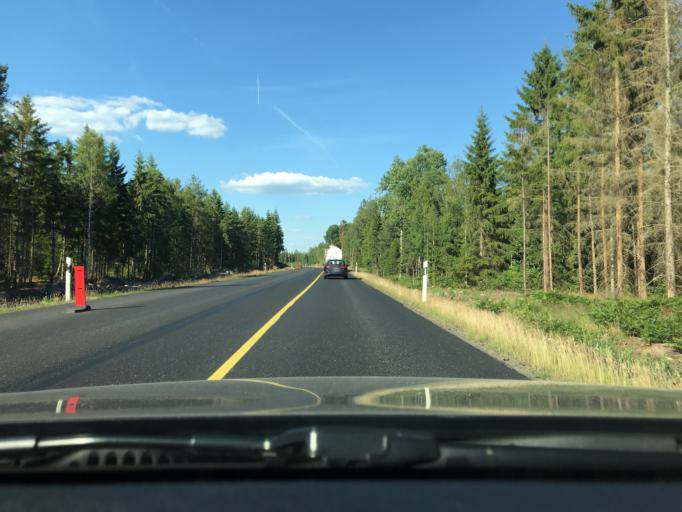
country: SE
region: Kronoberg
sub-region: Almhults Kommun
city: AElmhult
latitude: 56.6243
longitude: 14.2483
